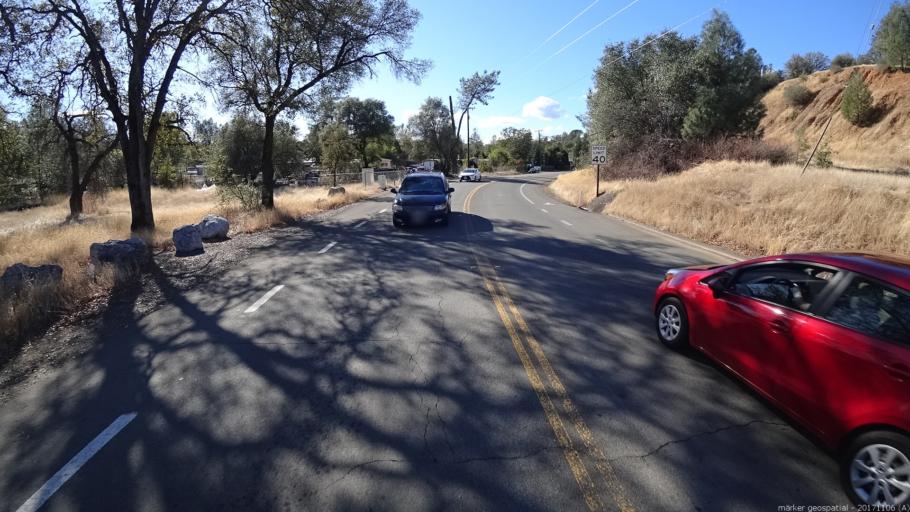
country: US
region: California
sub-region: Shasta County
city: Palo Cedro
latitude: 40.5881
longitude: -122.3069
